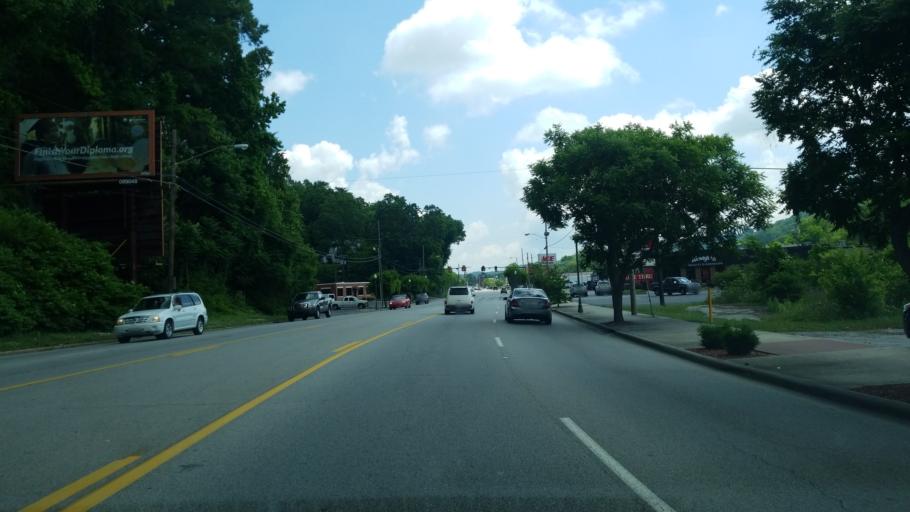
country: US
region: Tennessee
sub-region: Hamilton County
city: Red Bank
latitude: 35.0847
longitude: -85.3171
